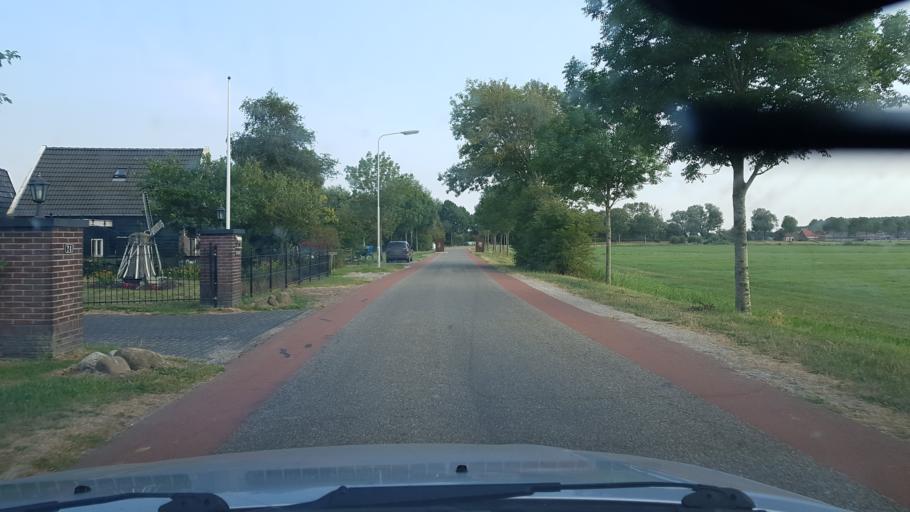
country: NL
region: Friesland
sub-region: Gemeente Ferwerderadiel
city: Burdaard
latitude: 53.3120
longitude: 5.8776
